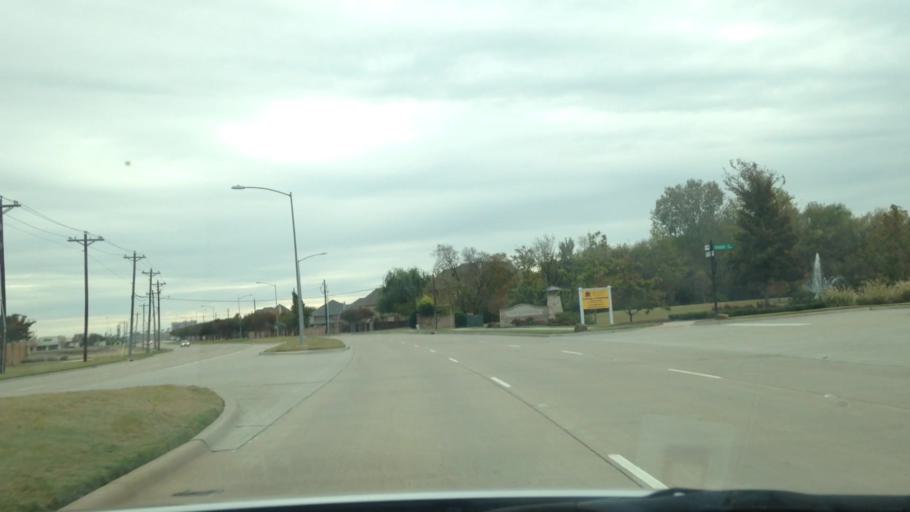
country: US
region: Texas
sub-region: Collin County
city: Allen
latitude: 33.1301
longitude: -96.6822
